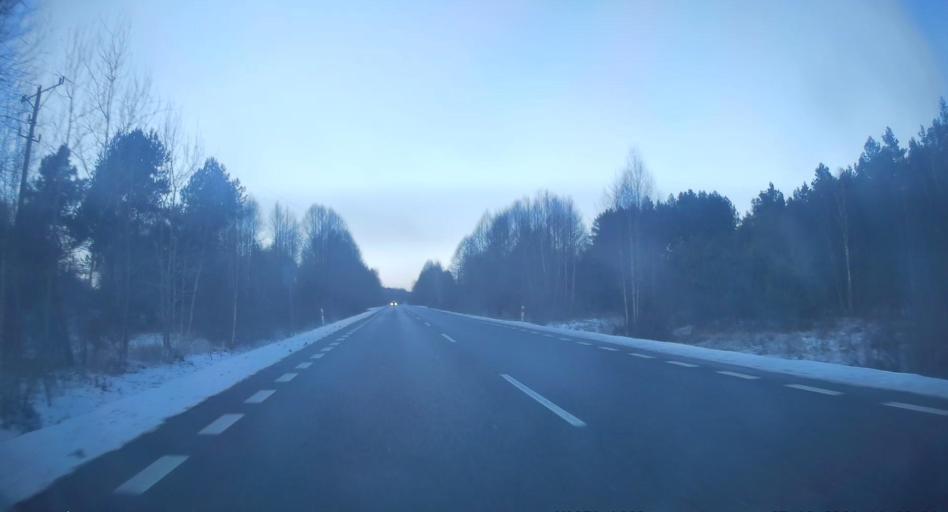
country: PL
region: Swietokrzyskie
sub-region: Powiat konecki
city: Ruda Maleniecka
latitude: 51.1299
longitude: 20.2535
